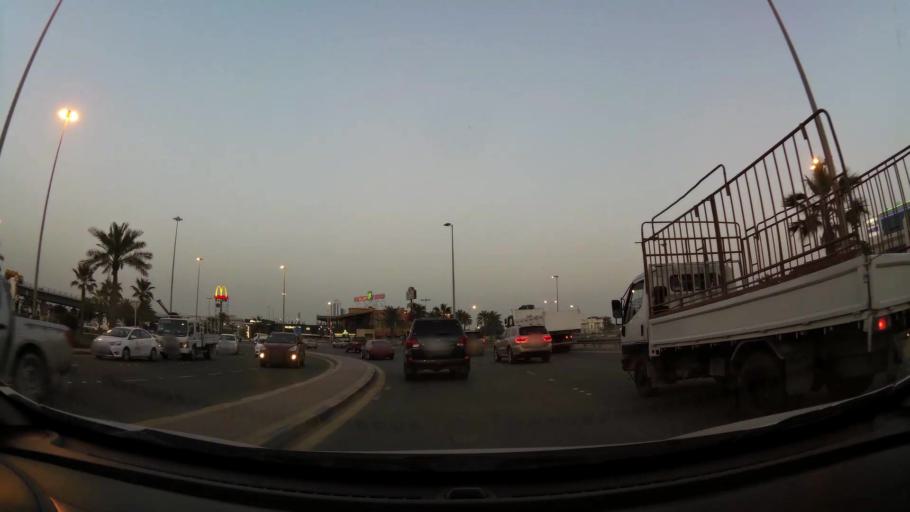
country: BH
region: Manama
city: Manama
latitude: 26.2034
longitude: 50.5668
